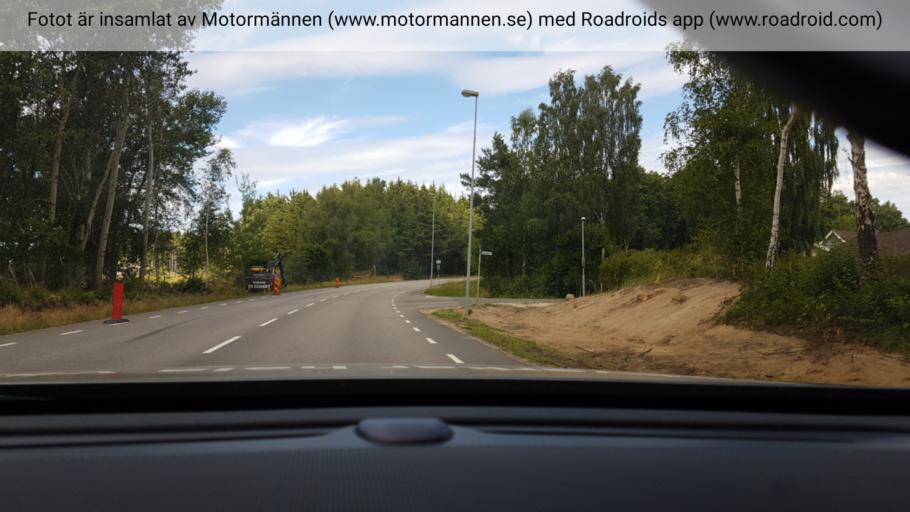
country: SE
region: Skane
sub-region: Hassleholms Kommun
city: Hassleholm
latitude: 56.1758
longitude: 13.7774
